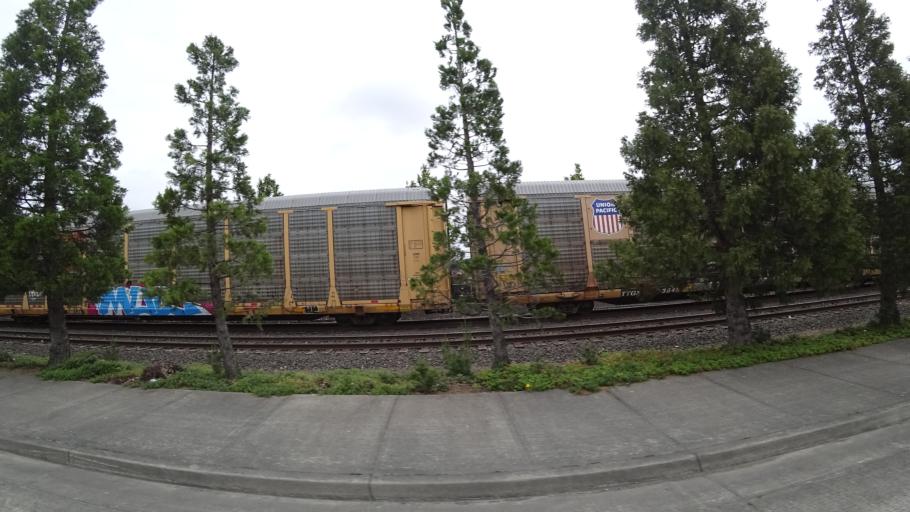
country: US
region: Washington
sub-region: Clark County
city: Lake Shore
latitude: 45.6315
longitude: -122.7473
